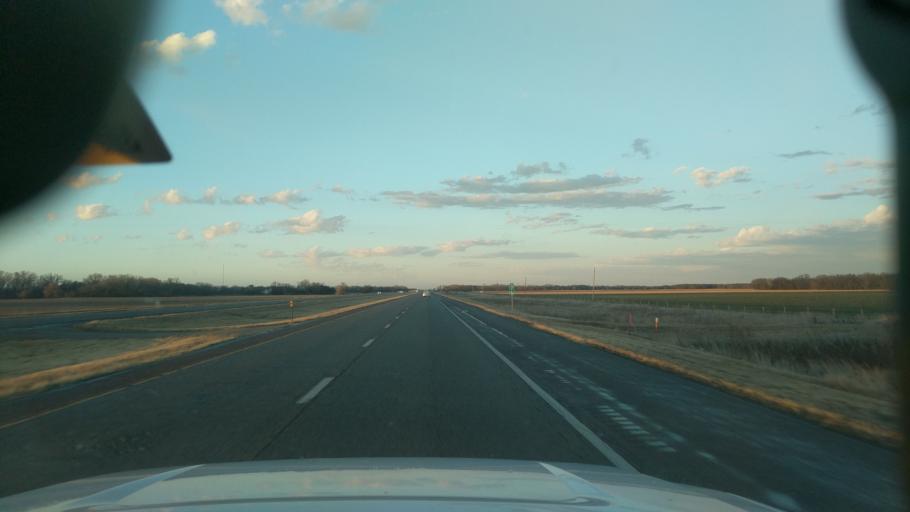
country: US
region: Kansas
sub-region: McPherson County
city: Lindsborg
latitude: 38.5939
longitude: -97.6211
